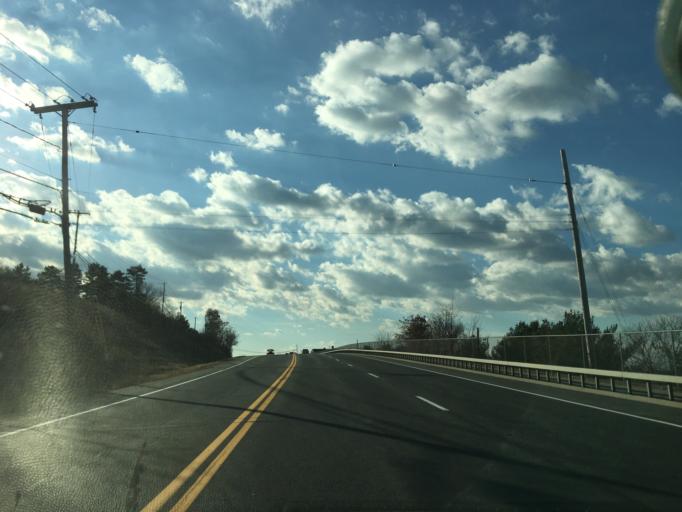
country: US
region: New York
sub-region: Rensselaer County
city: Hampton Manor
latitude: 42.6361
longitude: -73.7009
